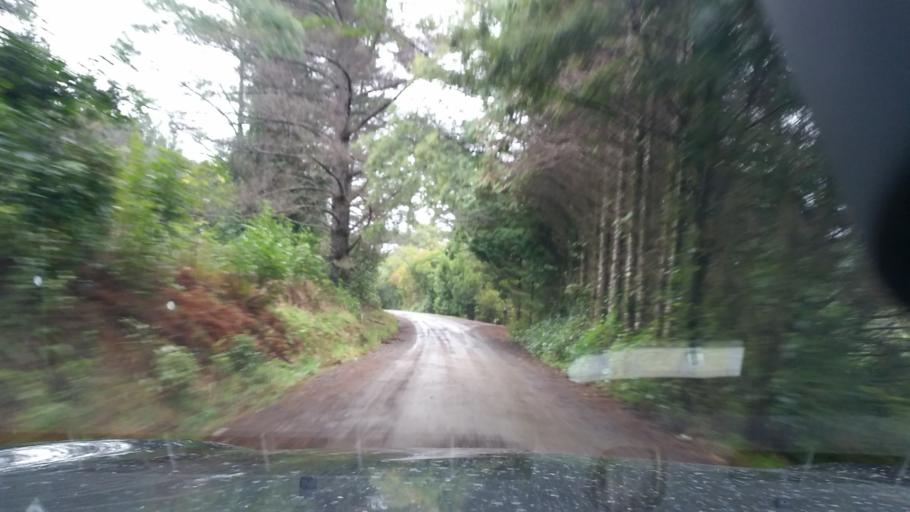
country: NZ
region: Nelson
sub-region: Nelson City
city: Nelson
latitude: -41.3559
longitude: 173.6275
